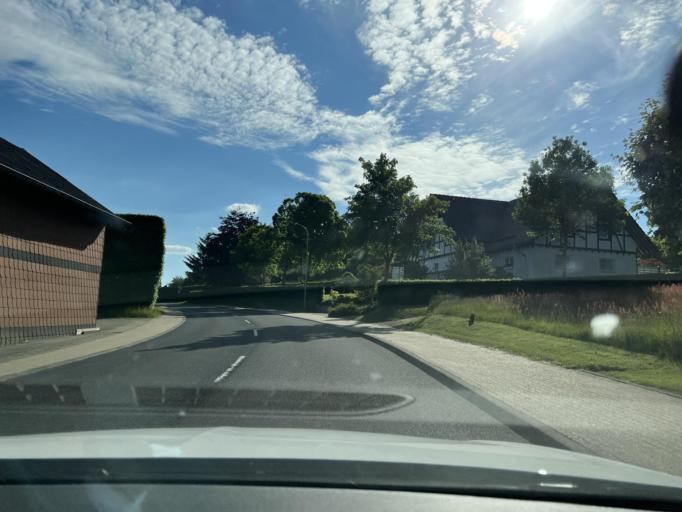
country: DE
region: North Rhine-Westphalia
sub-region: Regierungsbezirk Koln
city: Monschau
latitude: 50.5747
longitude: 6.2260
